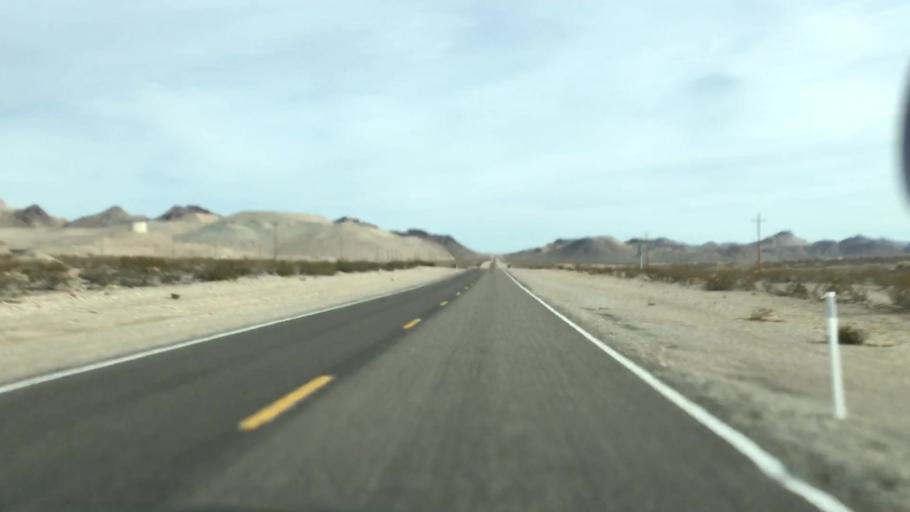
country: US
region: Nevada
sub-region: Nye County
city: Beatty
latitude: 36.8790
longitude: -116.8204
